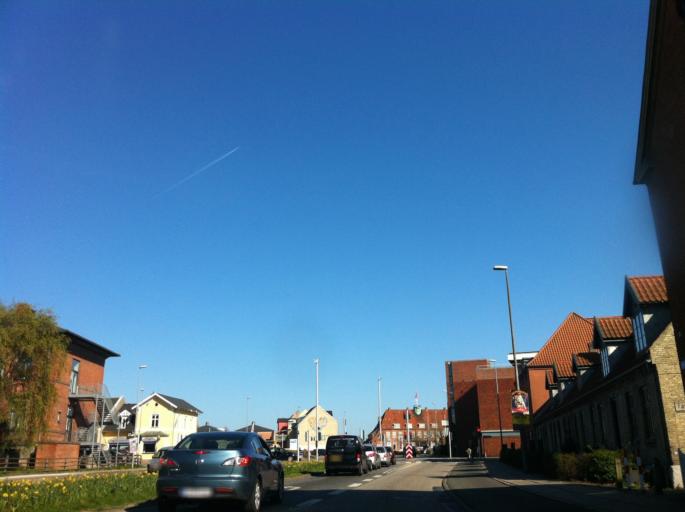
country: DK
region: Zealand
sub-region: Naestved Kommune
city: Naestved
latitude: 55.2344
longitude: 11.7590
